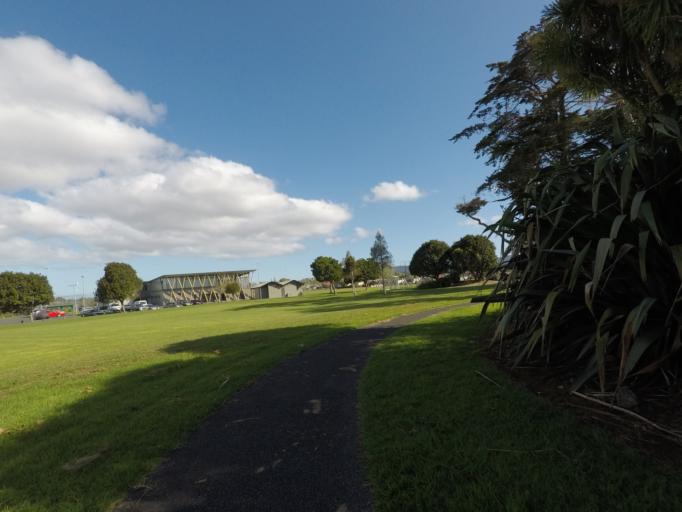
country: NZ
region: Auckland
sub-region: Auckland
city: Rosebank
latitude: -36.8586
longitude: 174.6046
